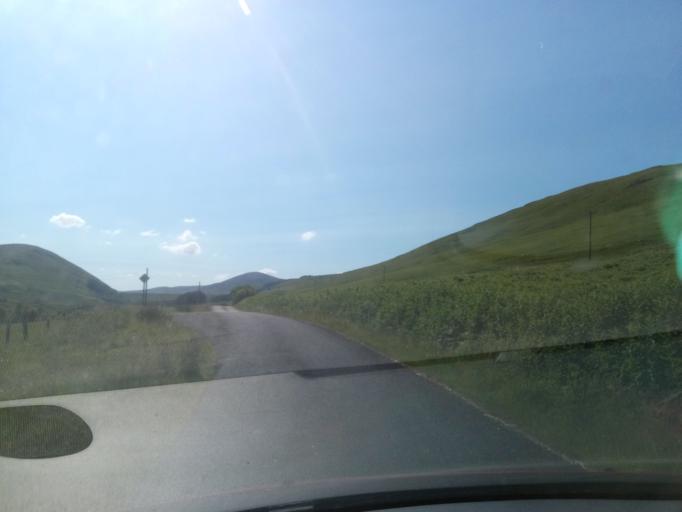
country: GB
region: Scotland
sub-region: The Scottish Borders
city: Peebles
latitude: 55.4981
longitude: -3.2231
